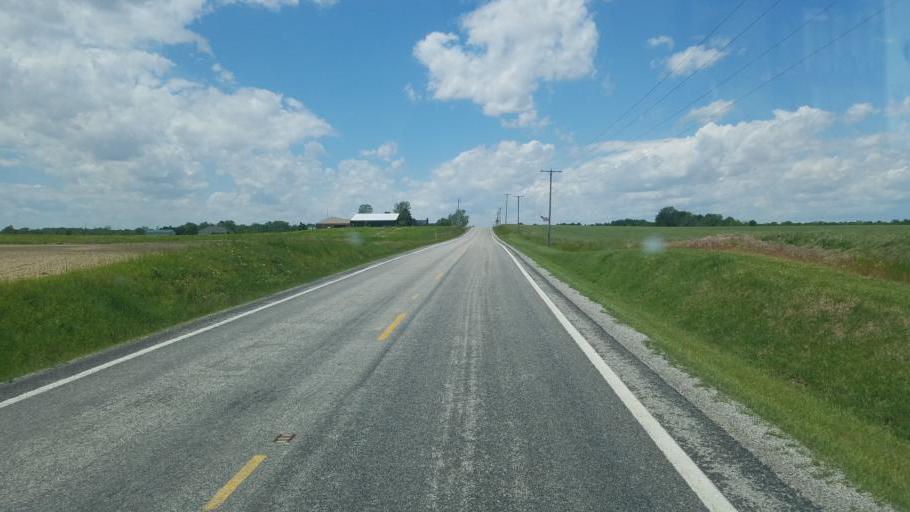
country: US
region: Ohio
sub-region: Huron County
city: Willard
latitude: 41.1052
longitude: -82.7126
